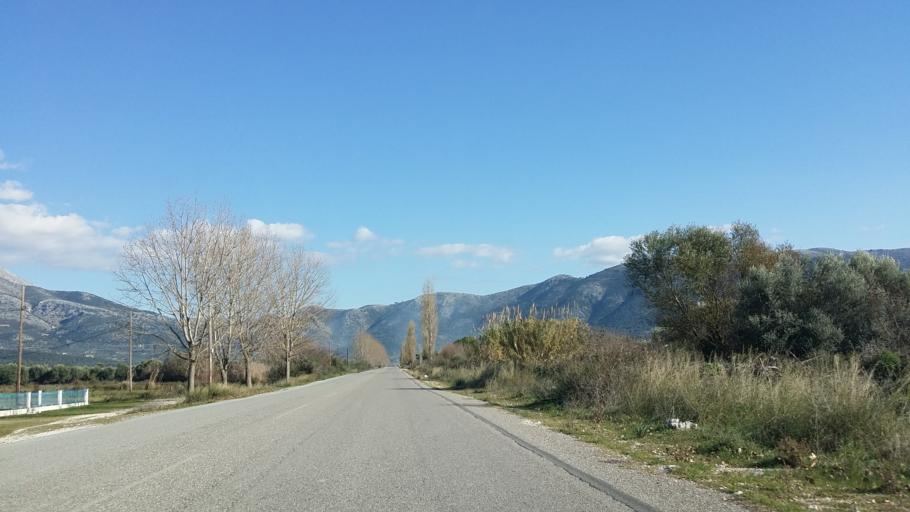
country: GR
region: West Greece
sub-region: Nomos Aitolias kai Akarnanias
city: Kandila
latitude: 38.6752
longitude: 20.9525
